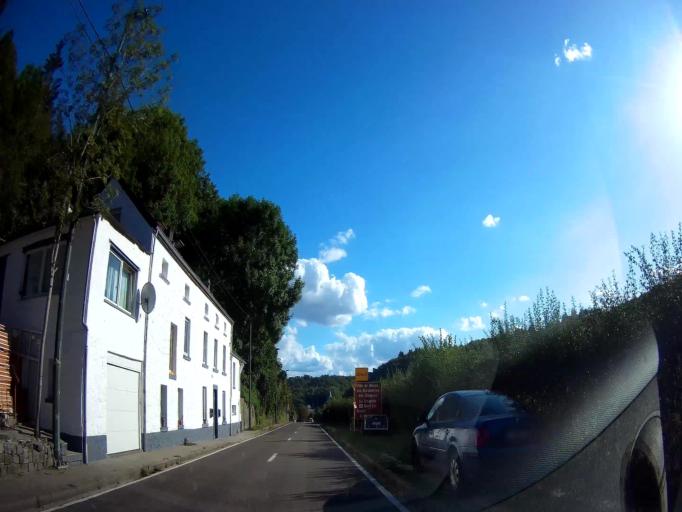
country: BE
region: Wallonia
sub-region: Province de Namur
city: Dinant
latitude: 50.2810
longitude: 4.8968
